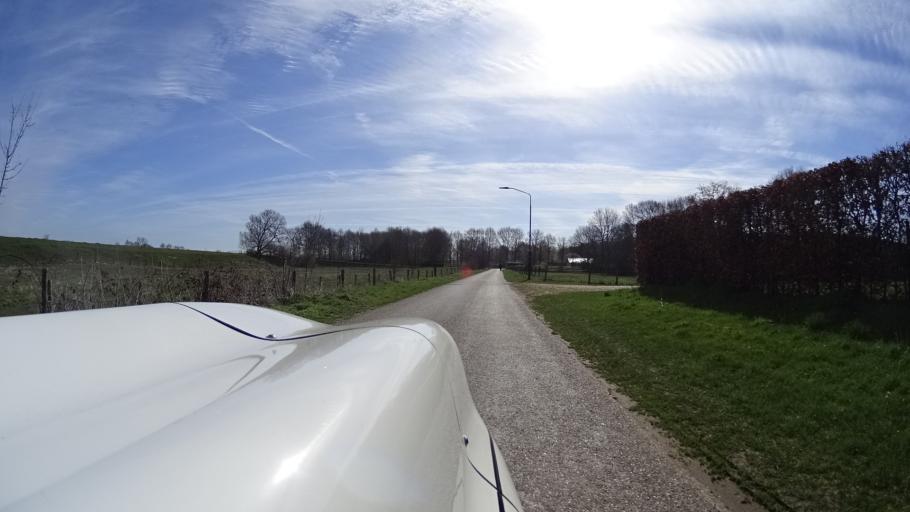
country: NL
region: Limburg
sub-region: Gemeente Gennep
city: Gennep
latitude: 51.7070
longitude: 5.9359
